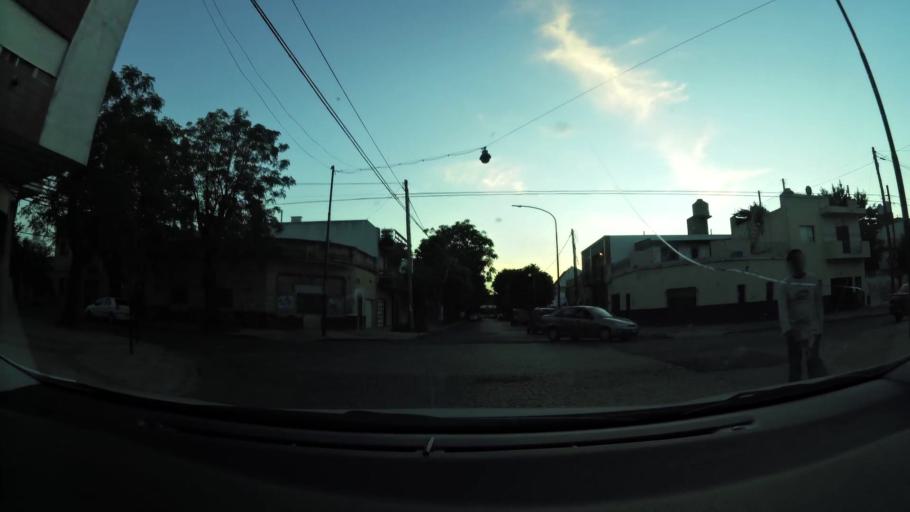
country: AR
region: Buenos Aires F.D.
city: Villa Lugano
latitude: -34.6769
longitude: -58.4736
